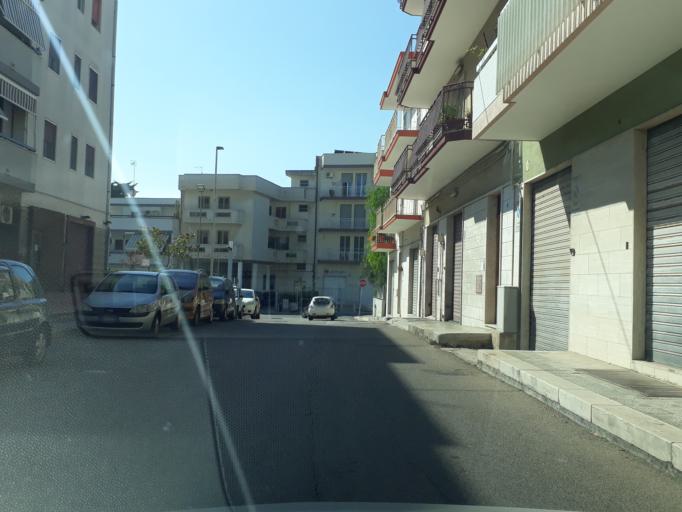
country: IT
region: Apulia
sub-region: Provincia di Bari
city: Monopoli
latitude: 40.9474
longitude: 17.2935
